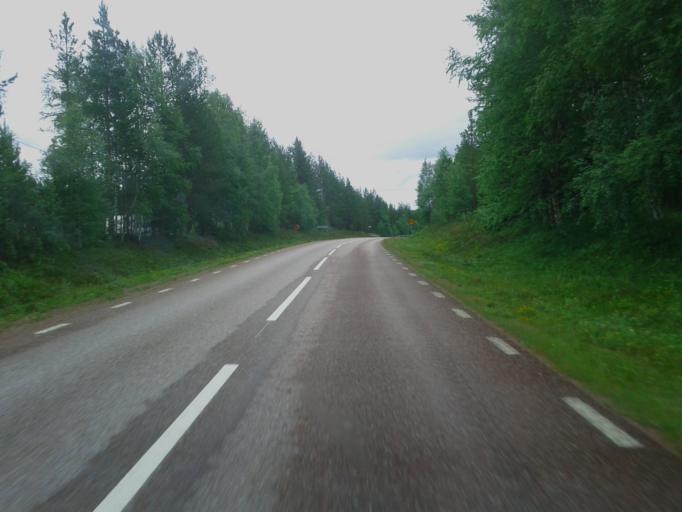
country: NO
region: Hedmark
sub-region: Trysil
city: Innbygda
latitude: 61.7230
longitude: 12.9967
